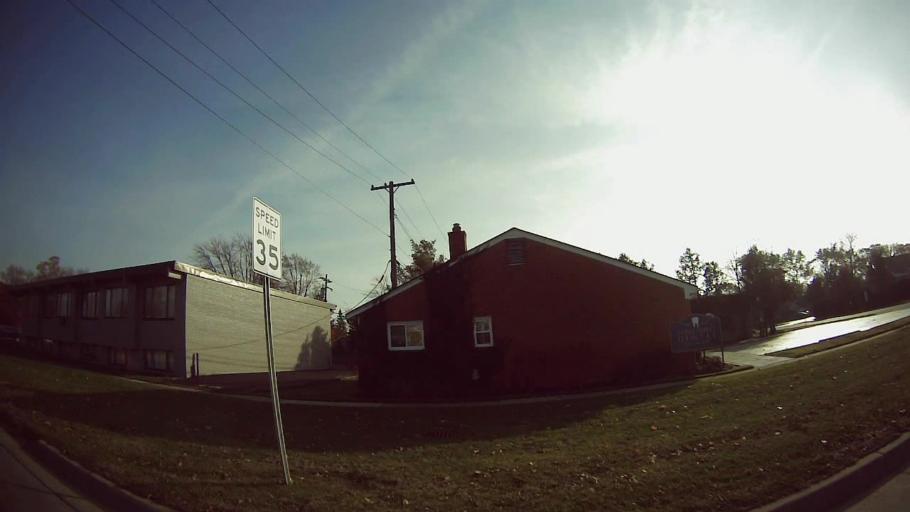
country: US
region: Michigan
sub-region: Oakland County
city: Beverly Hills
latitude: 42.5316
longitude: -83.2144
